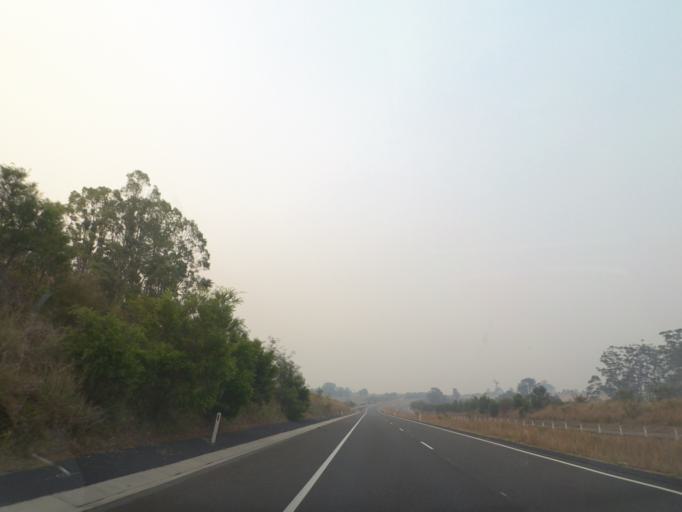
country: AU
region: New South Wales
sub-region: Nambucca Shire
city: Macksville
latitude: -30.7639
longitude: 152.9040
